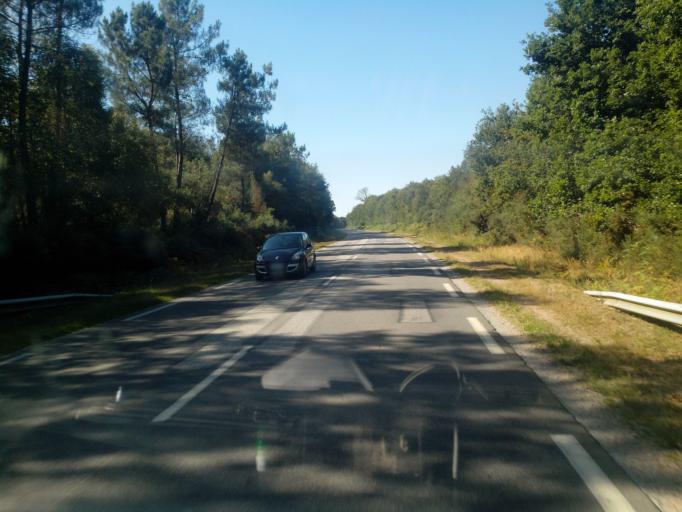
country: FR
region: Brittany
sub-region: Departement du Morbihan
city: Molac
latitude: 47.7632
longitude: -2.4459
